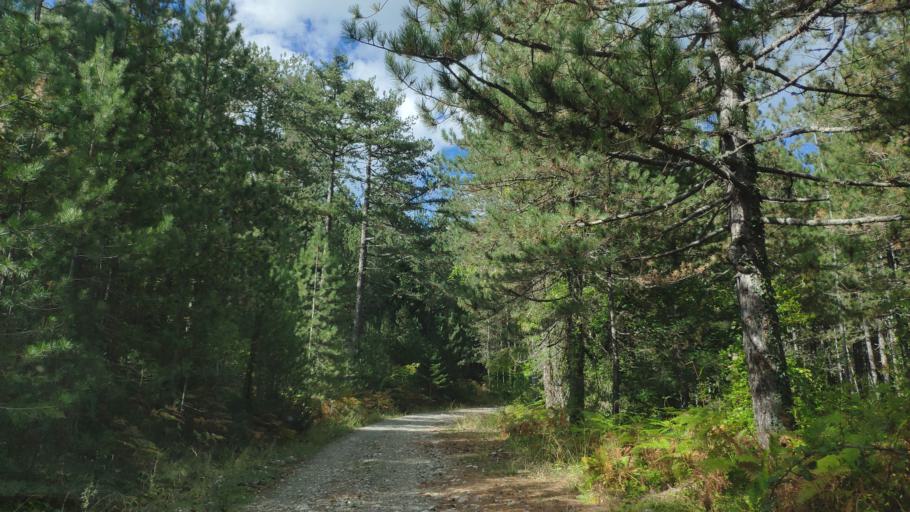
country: GR
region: Epirus
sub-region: Nomos Ioanninon
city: Metsovo
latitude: 39.8898
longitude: 21.2504
